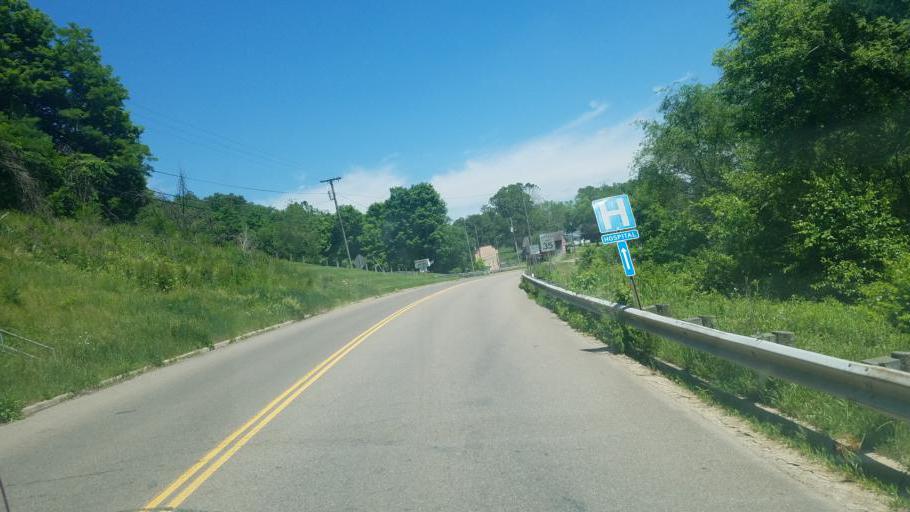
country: US
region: Ohio
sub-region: Coshocton County
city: Coshocton
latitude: 40.2749
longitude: -81.8856
